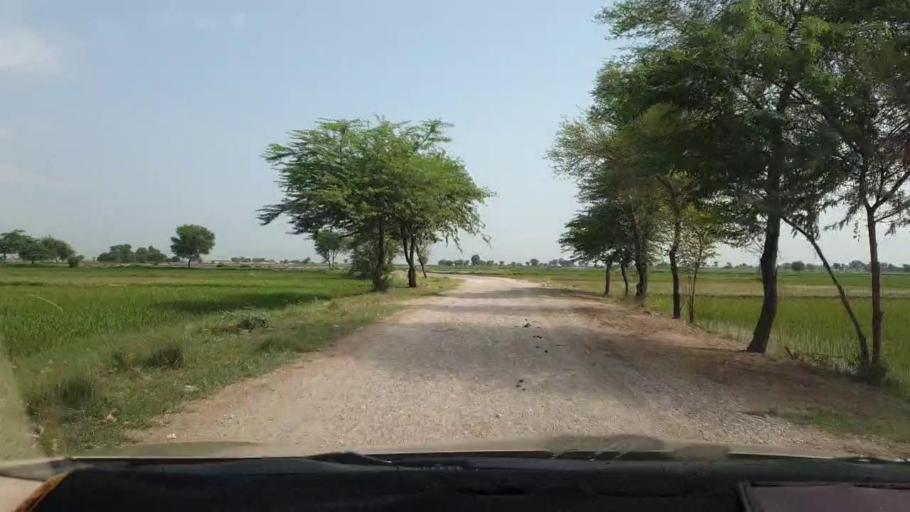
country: PK
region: Sindh
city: Larkana
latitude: 27.6767
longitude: 68.2203
